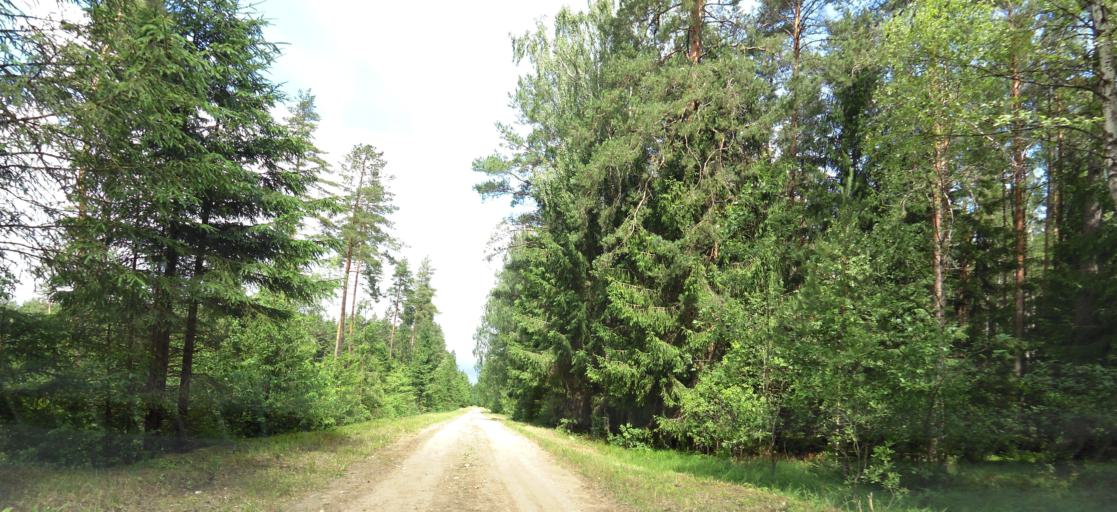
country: LT
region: Panevezys
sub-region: Birzai
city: Birzai
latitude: 56.2674
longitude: 24.7528
